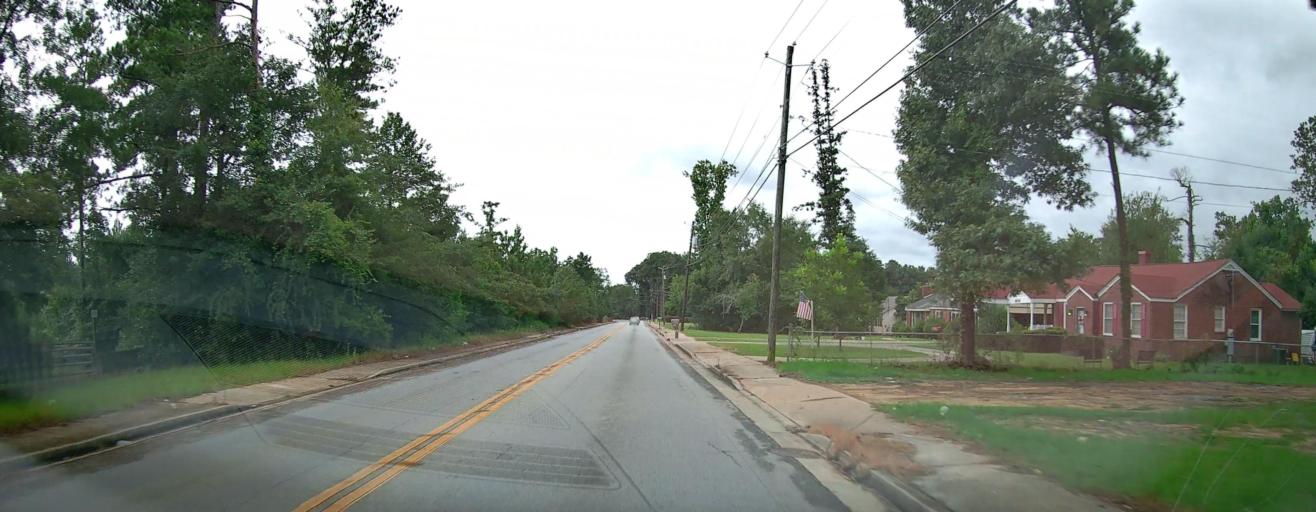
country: US
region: Georgia
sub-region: Bibb County
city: Macon
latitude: 32.8012
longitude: -83.7001
